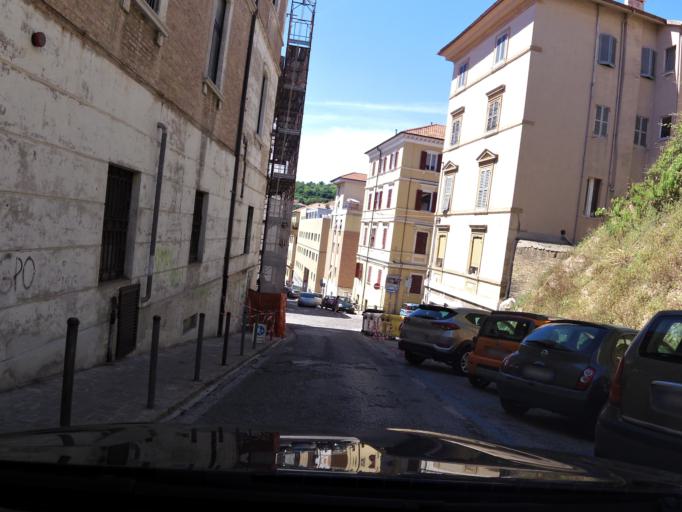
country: IT
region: The Marches
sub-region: Provincia di Ancona
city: Le Grazie di Ancona
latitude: 43.6195
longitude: 13.5139
